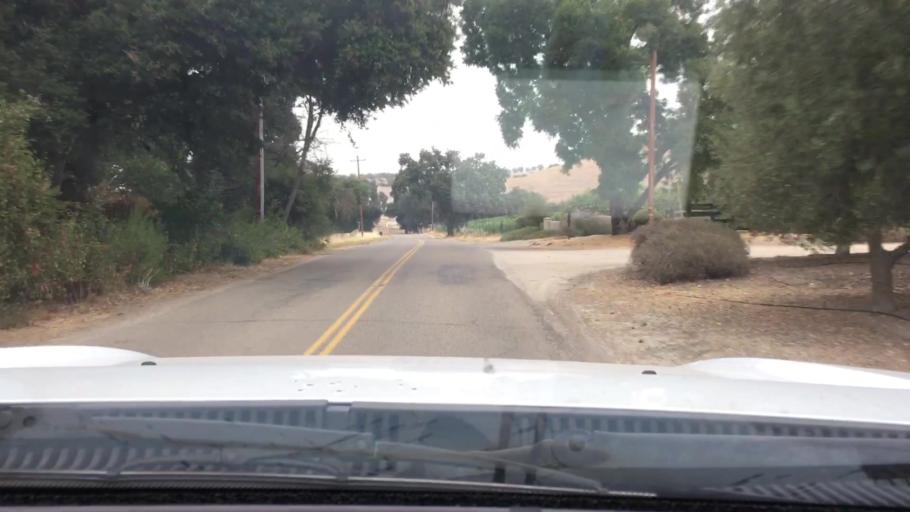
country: US
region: California
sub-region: San Luis Obispo County
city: Atascadero
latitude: 35.5299
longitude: -120.6189
